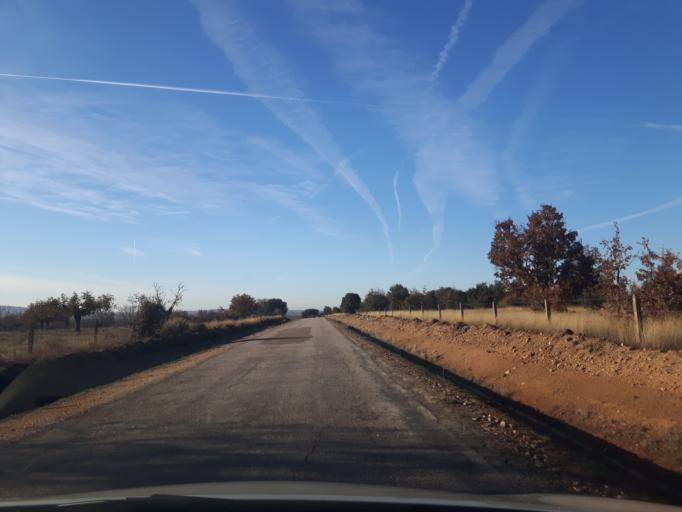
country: ES
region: Castille and Leon
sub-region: Provincia de Salamanca
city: Cerralbo
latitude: 40.9532
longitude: -6.6035
